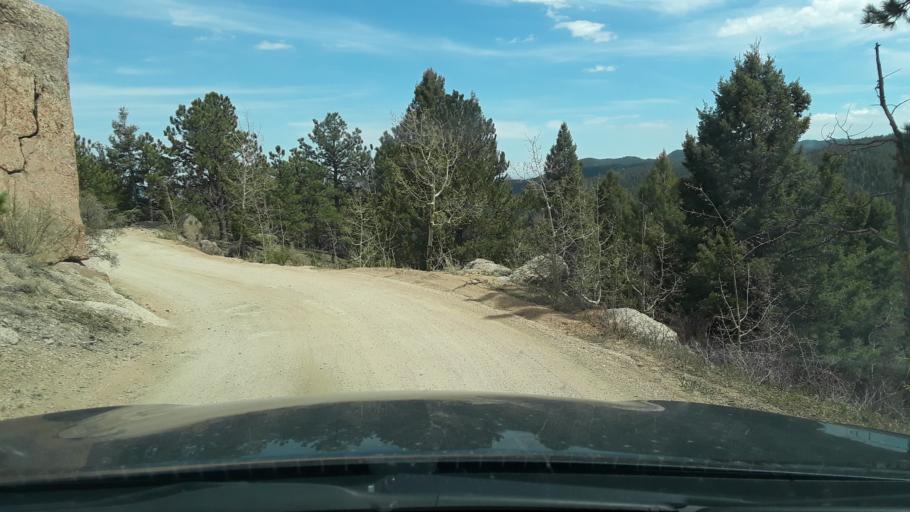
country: US
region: Colorado
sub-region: El Paso County
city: Palmer Lake
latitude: 39.0699
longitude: -104.9522
